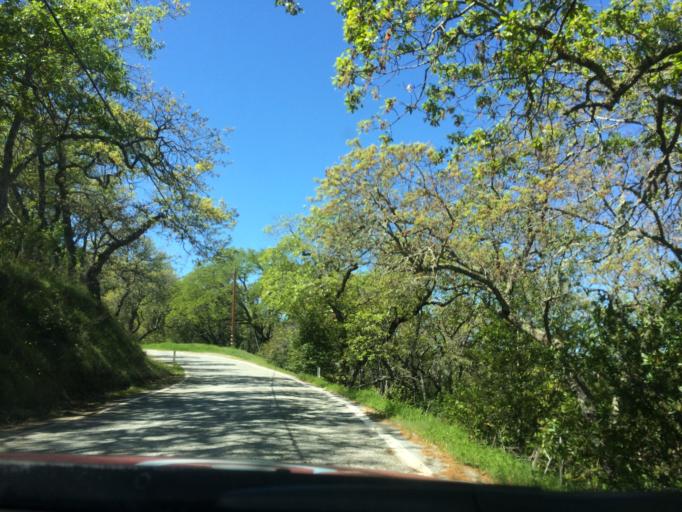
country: US
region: California
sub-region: Santa Clara County
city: Morgan Hill
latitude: 37.1703
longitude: -121.5703
